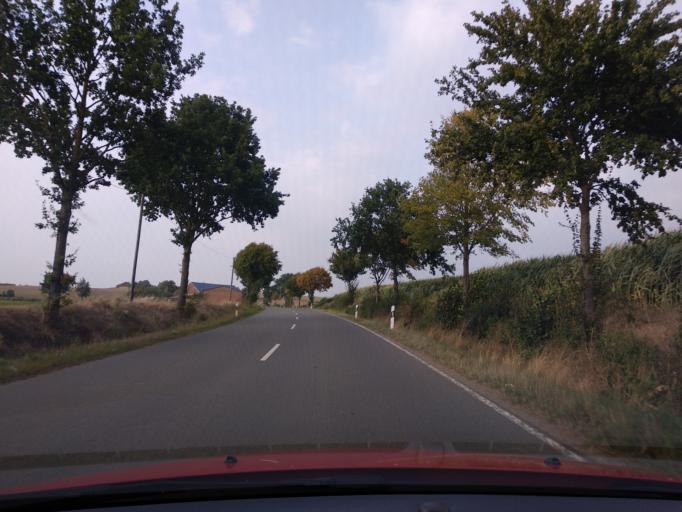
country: DE
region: Hesse
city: Liebenau
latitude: 51.5390
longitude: 9.2895
